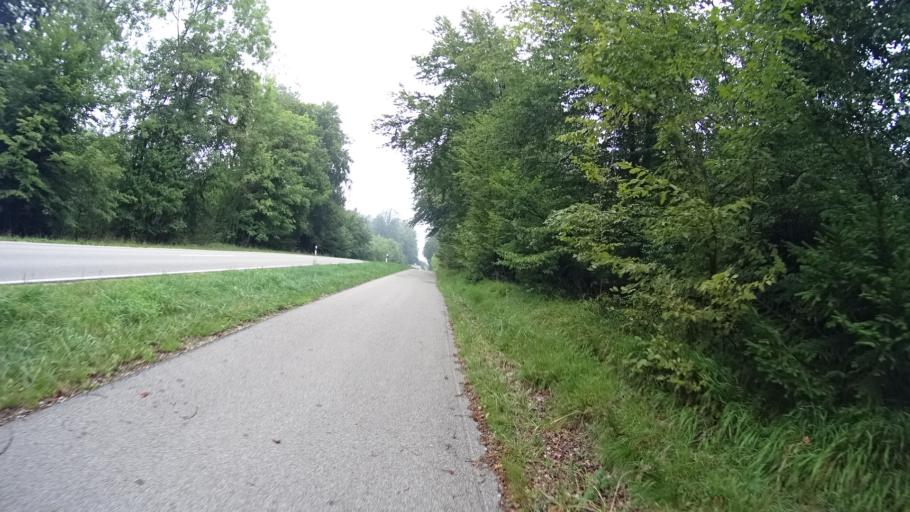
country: DE
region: Bavaria
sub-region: Upper Bavaria
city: Denkendorf
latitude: 48.9008
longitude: 11.4570
